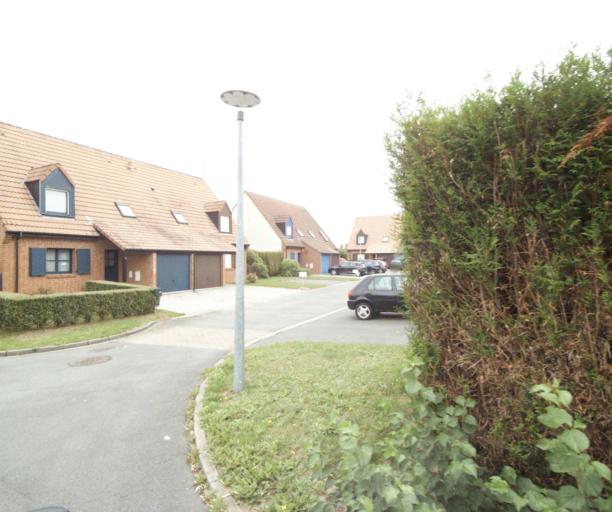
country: FR
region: Nord-Pas-de-Calais
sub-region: Departement du Nord
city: Ronchin
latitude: 50.5987
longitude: 3.0852
